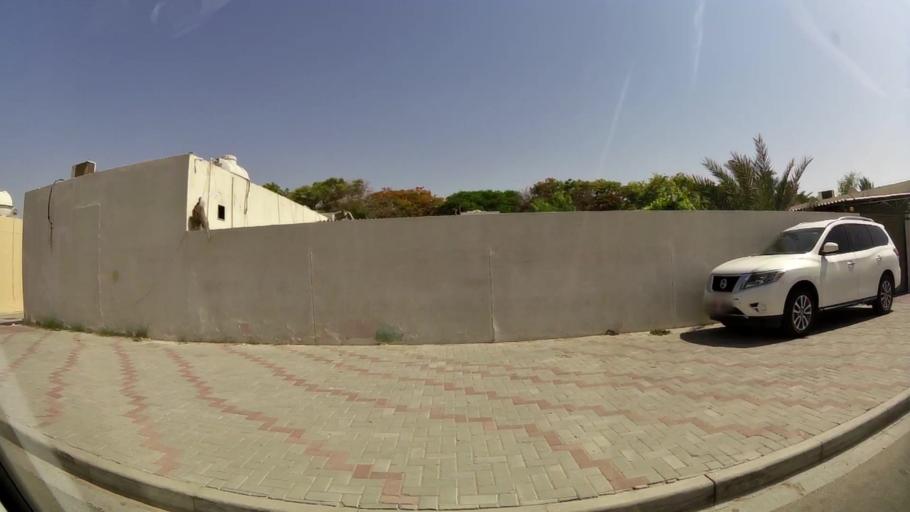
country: AE
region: Ash Shariqah
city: Sharjah
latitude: 25.2688
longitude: 55.3607
